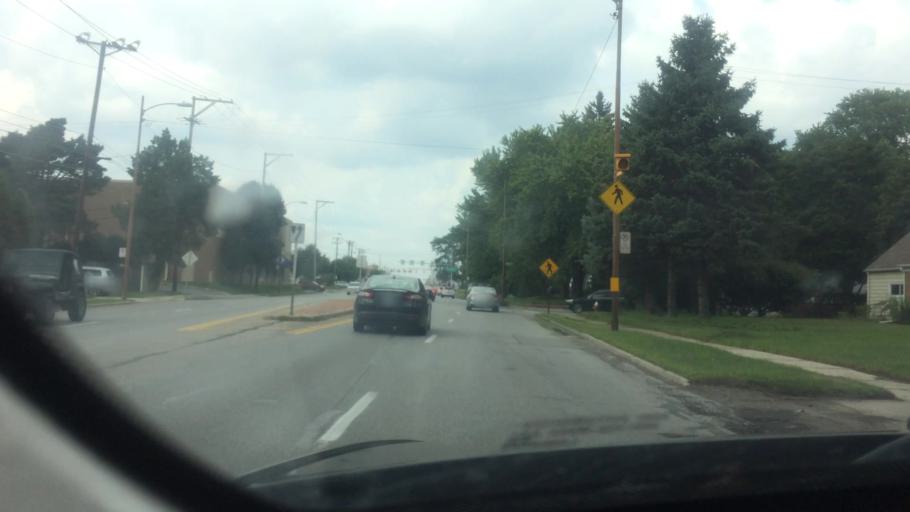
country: US
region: Ohio
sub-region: Lucas County
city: Ottawa Hills
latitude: 41.6745
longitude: -83.6225
